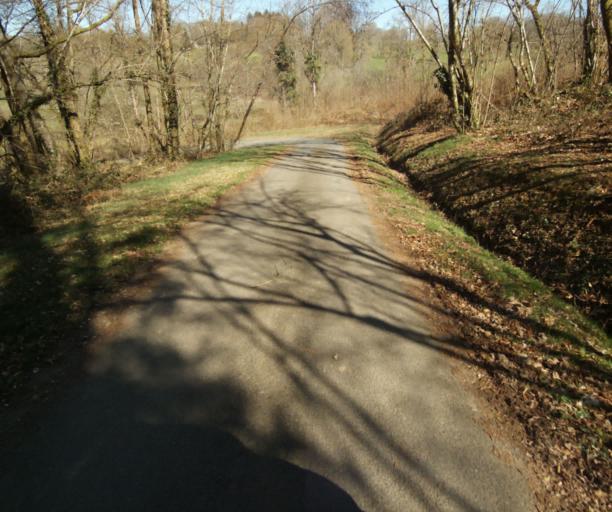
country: FR
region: Limousin
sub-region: Departement de la Correze
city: Saint-Clement
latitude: 45.3893
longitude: 1.6639
